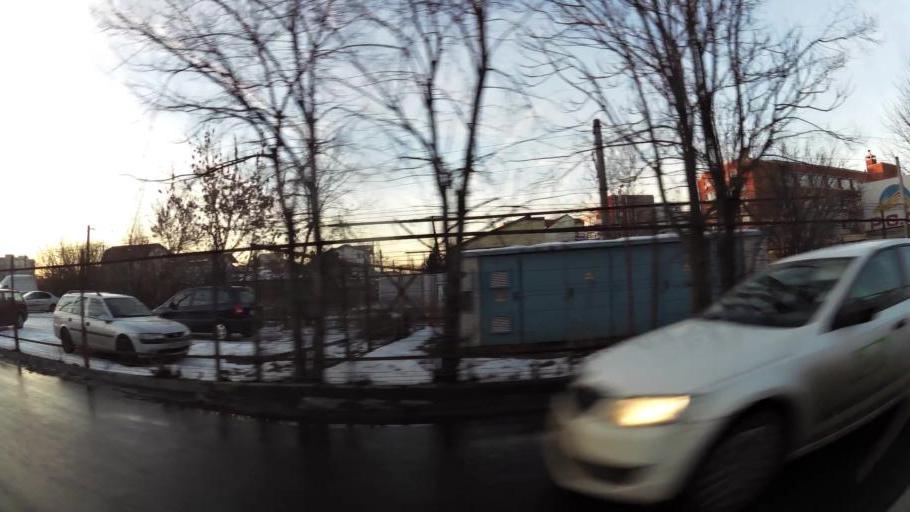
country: RO
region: Ilfov
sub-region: Comuna Fundeni-Dobroesti
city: Fundeni
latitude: 44.4468
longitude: 26.1497
